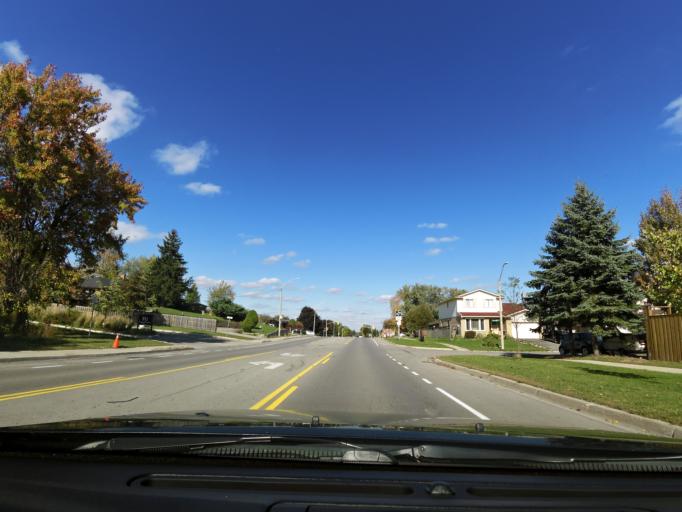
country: CA
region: Ontario
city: Ancaster
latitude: 43.2222
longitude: -79.9168
